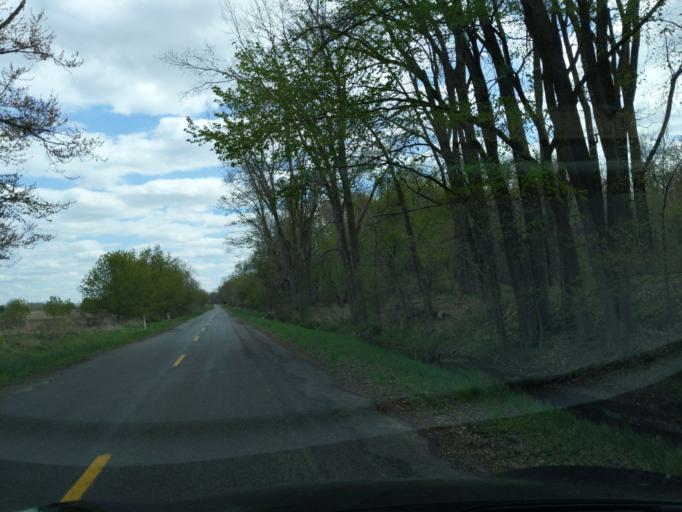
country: US
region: Michigan
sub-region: Eaton County
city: Eaton Rapids
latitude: 42.5189
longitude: -84.5421
